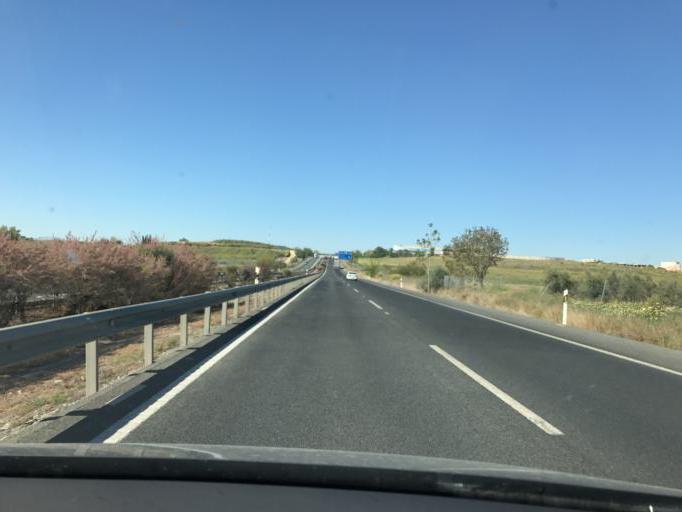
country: ES
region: Andalusia
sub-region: Provincia de Granada
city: Cijuela
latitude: 37.1932
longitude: -3.8214
